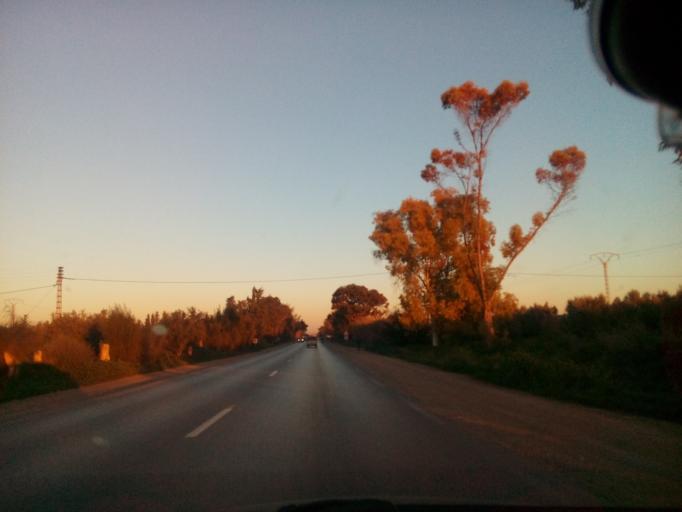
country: DZ
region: Relizane
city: Relizane
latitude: 35.7246
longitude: 0.3763
